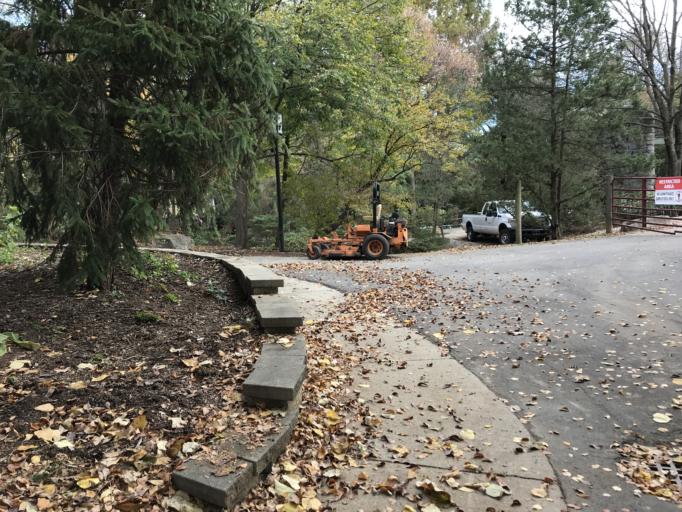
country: US
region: Kentucky
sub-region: Jefferson County
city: Audubon Park
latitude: 38.2040
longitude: -85.7058
